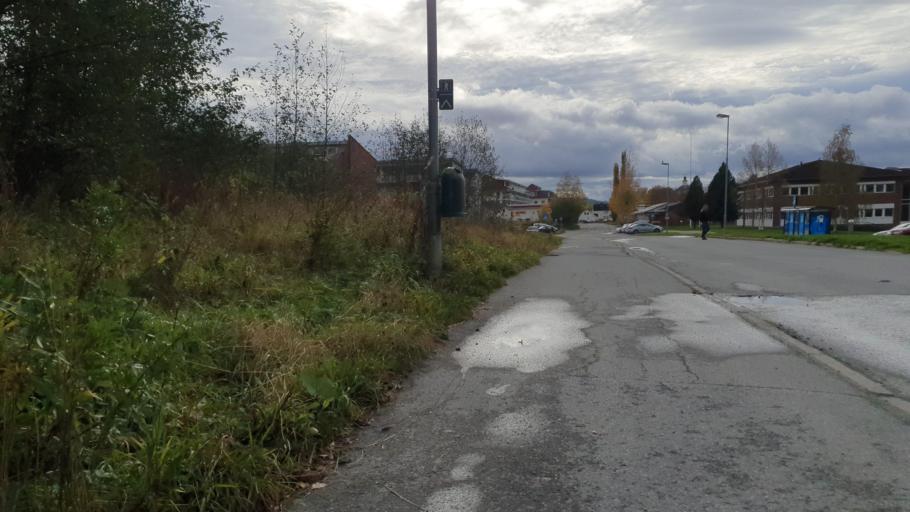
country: NO
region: Sor-Trondelag
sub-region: Klaebu
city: Klaebu
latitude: 63.3014
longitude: 10.4839
